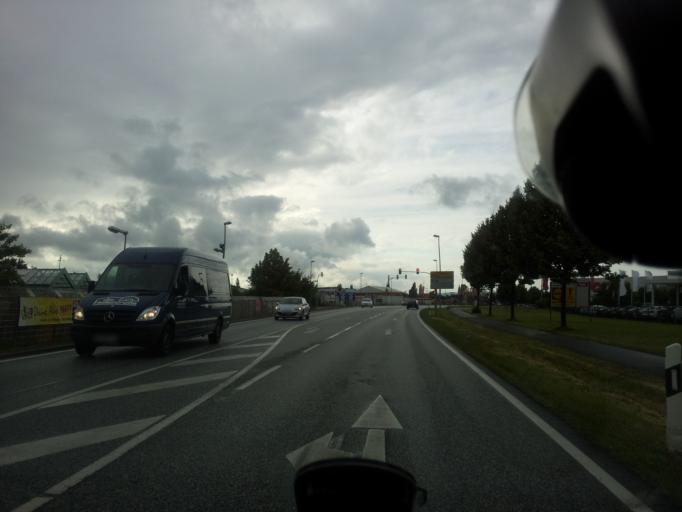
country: DE
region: Saxony-Anhalt
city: Harsleben
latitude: 51.8790
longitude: 11.0768
